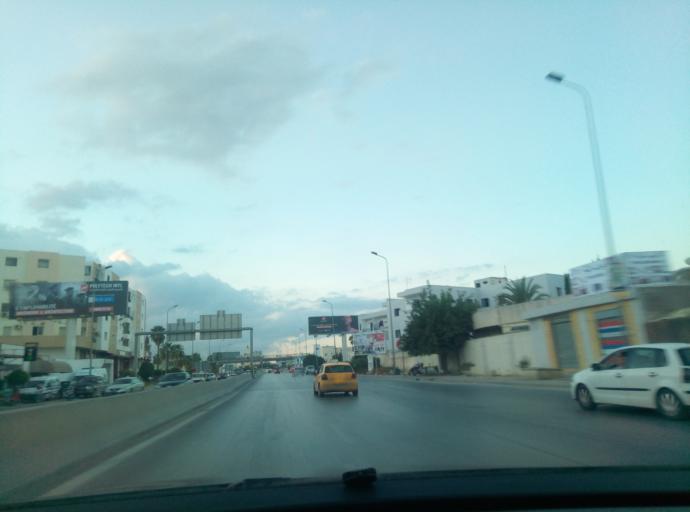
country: TN
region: Manouba
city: Manouba
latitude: 36.8050
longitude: 10.1188
